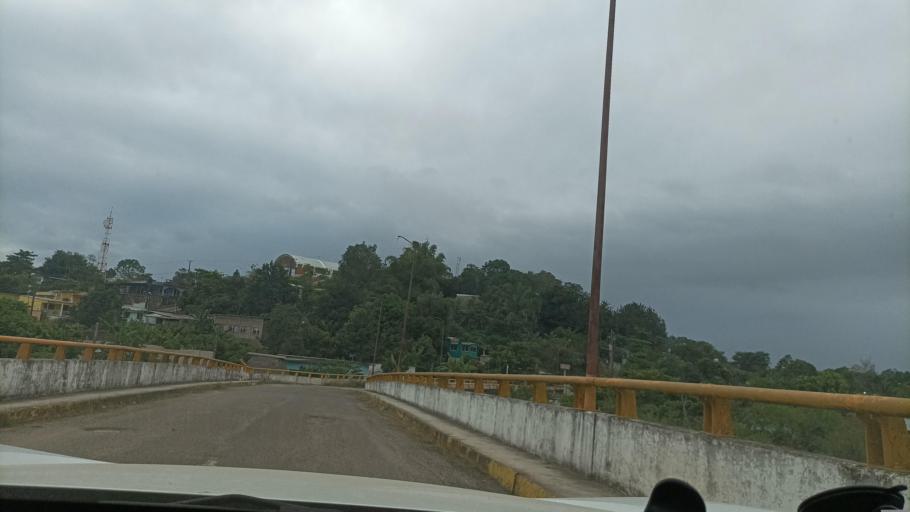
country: MX
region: Veracruz
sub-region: Jaltipan
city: Las Lomas de Tacamichapan
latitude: 17.8686
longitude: -94.7072
